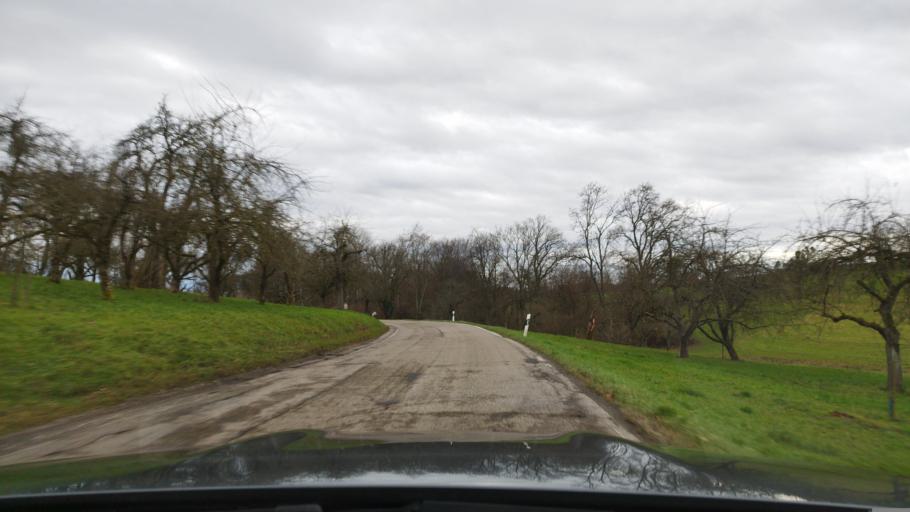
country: DE
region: Baden-Wuerttemberg
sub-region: Regierungsbezirk Stuttgart
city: Burgstetten
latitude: 48.9381
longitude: 9.3596
